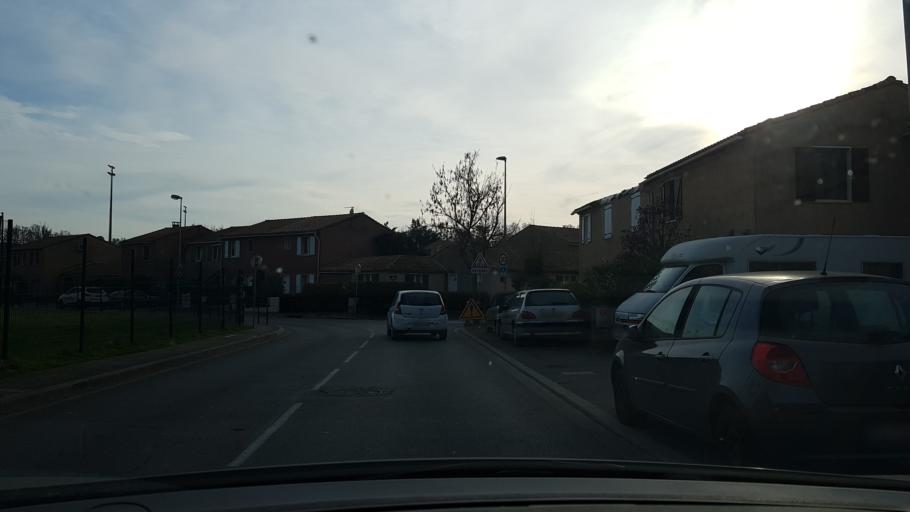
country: FR
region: Provence-Alpes-Cote d'Azur
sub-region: Departement des Bouches-du-Rhone
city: Bouc-Bel-Air
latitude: 43.4859
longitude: 5.4152
